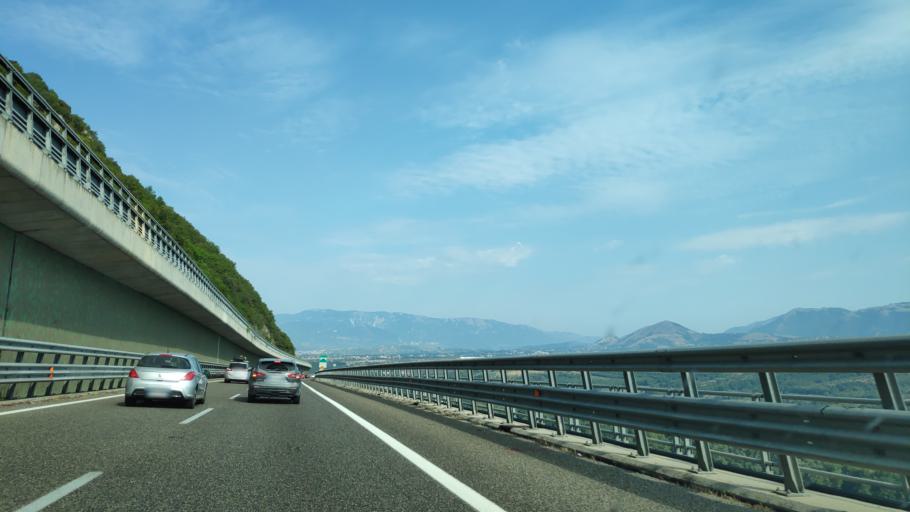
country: IT
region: Campania
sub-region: Provincia di Salerno
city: Sicignano degli Alburni
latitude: 40.5870
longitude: 15.3367
